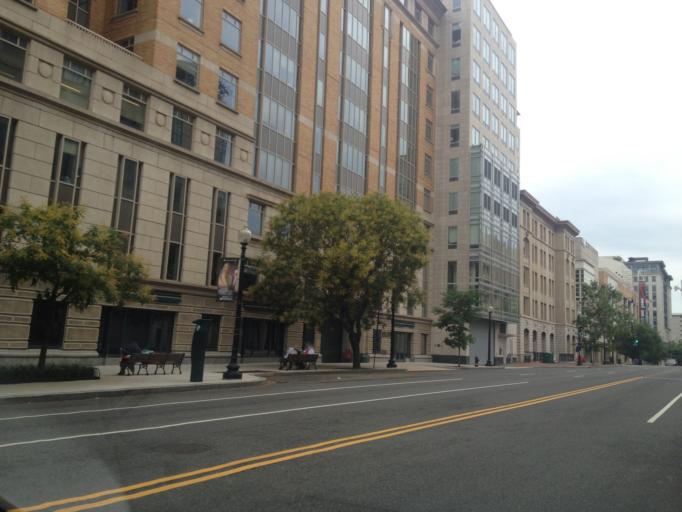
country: US
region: Washington, D.C.
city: Washington, D.C.
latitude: 38.8962
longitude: -77.0199
